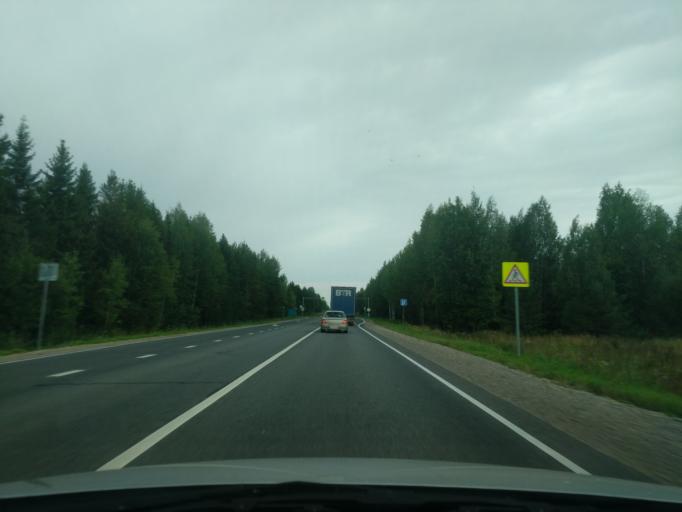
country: RU
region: Kirov
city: Kotel'nich
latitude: 58.4819
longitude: 48.5746
